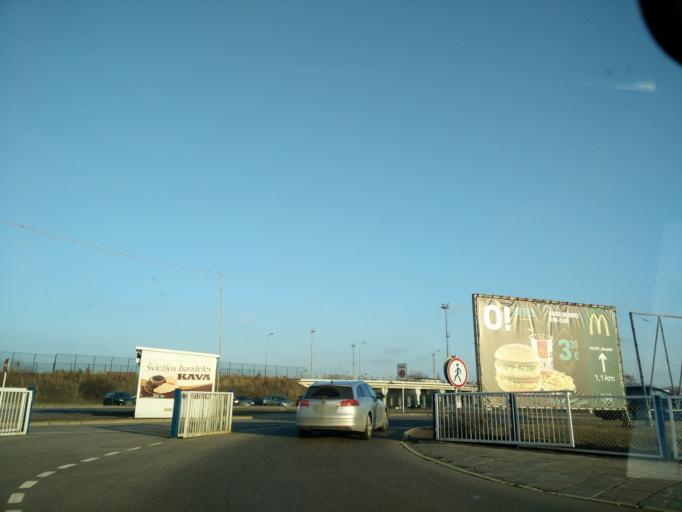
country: LT
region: Klaipedos apskritis
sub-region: Klaipeda
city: Klaipeda
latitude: 55.6885
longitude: 21.1393
